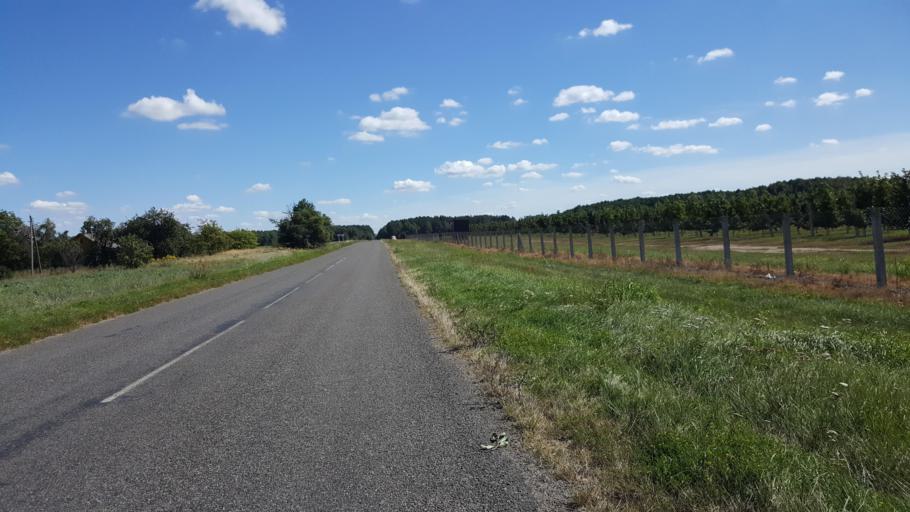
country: BY
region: Brest
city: Vysokaye
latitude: 52.2725
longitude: 23.3743
